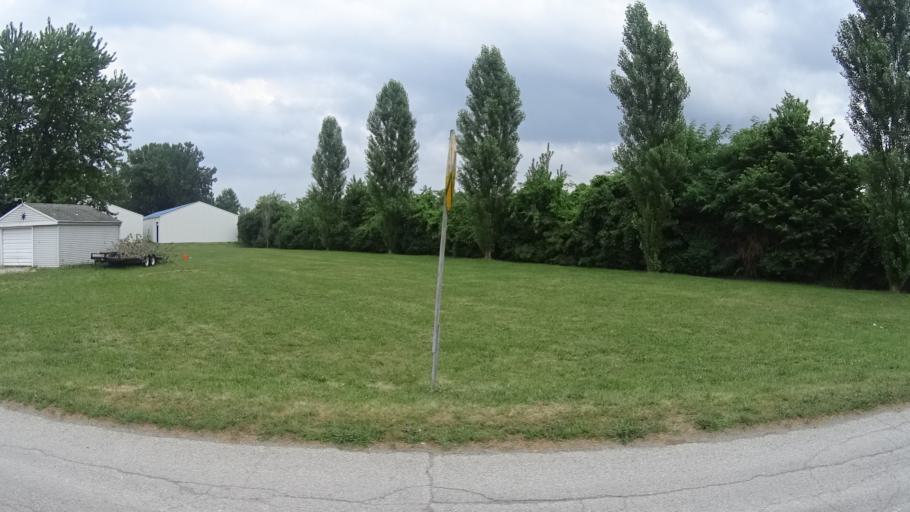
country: US
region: Ohio
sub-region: Erie County
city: Sandusky
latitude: 41.4447
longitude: -82.7378
